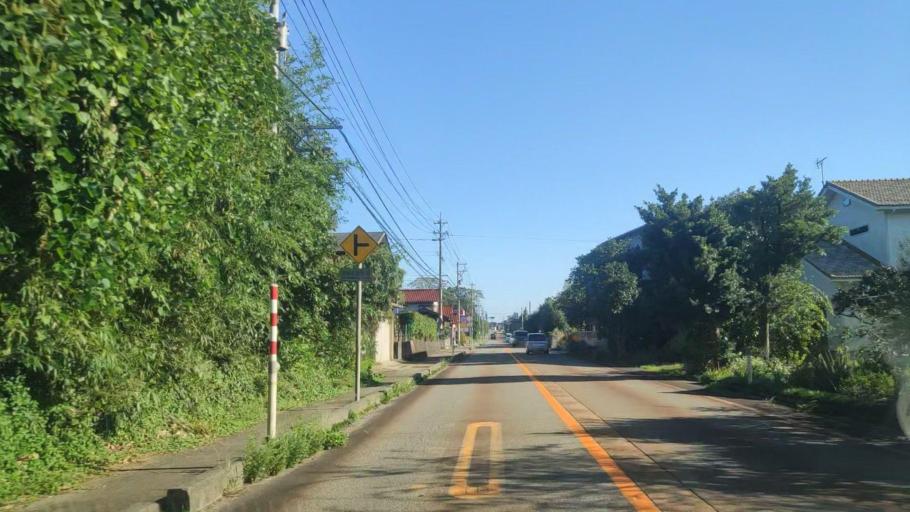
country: JP
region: Ishikawa
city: Hakui
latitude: 36.8378
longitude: 136.7627
